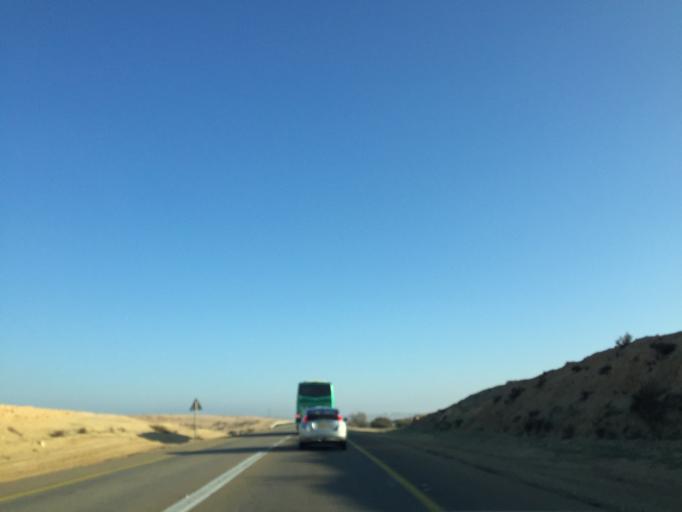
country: IL
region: Southern District
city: Yeroham
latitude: 31.0278
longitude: 34.9702
